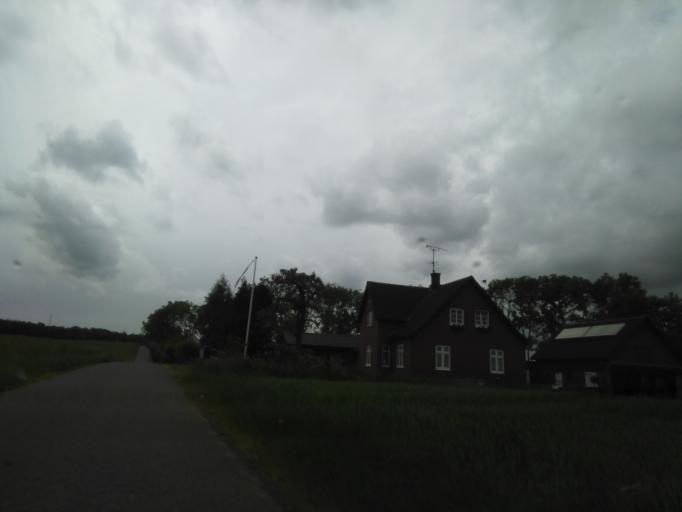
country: DK
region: Capital Region
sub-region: Bornholm Kommune
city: Nexo
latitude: 55.0996
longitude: 15.1285
